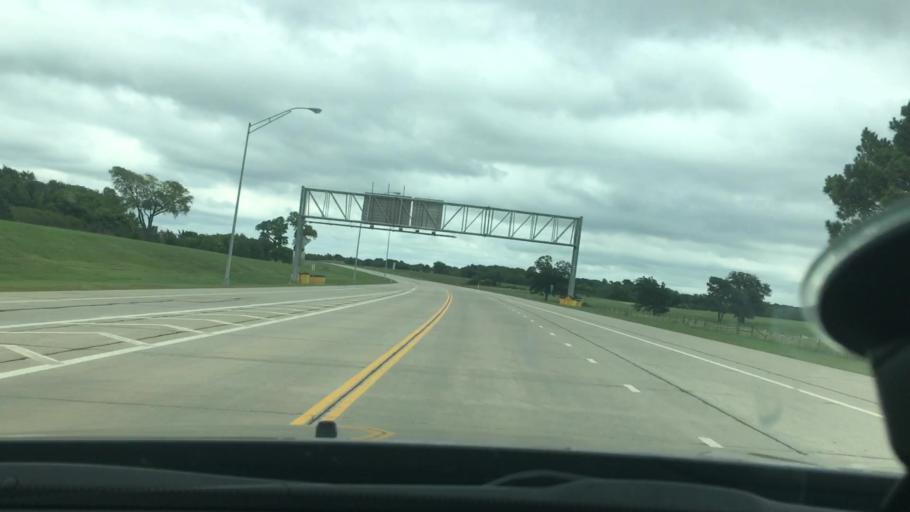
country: US
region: Oklahoma
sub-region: Murray County
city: Sulphur
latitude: 34.5684
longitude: -96.9282
